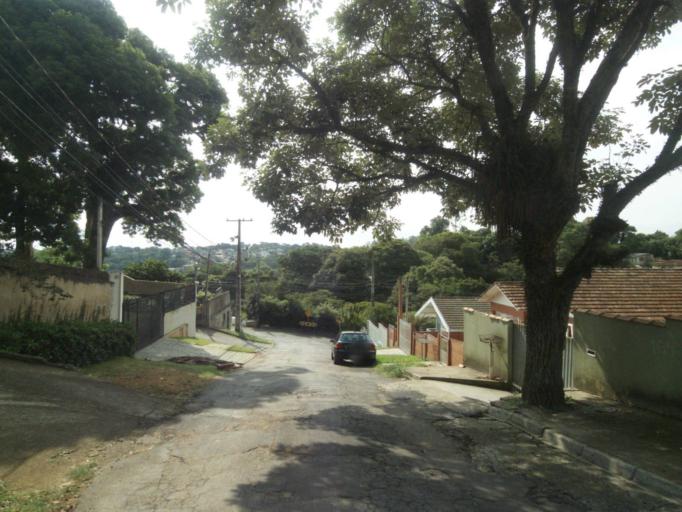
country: BR
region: Parana
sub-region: Curitiba
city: Curitiba
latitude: -25.4084
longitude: -49.3012
